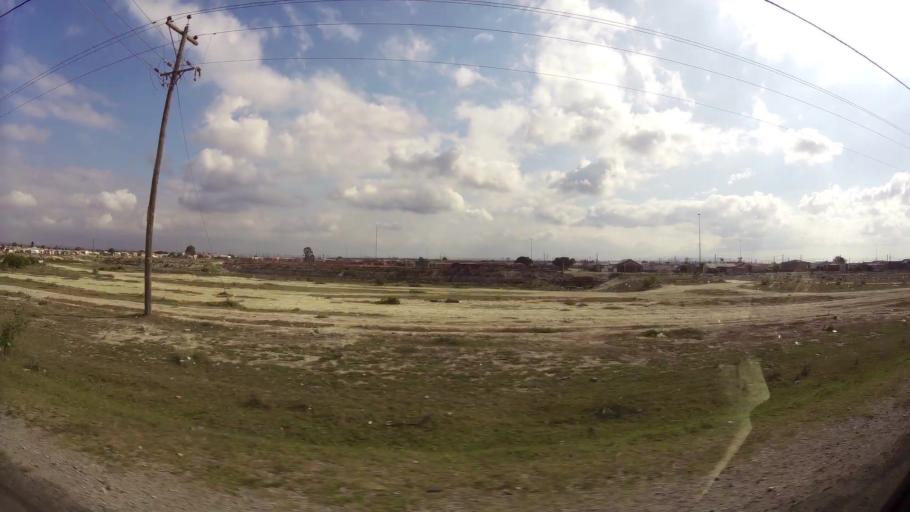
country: ZA
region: Eastern Cape
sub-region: Nelson Mandela Bay Metropolitan Municipality
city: Port Elizabeth
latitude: -33.7777
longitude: 25.5904
